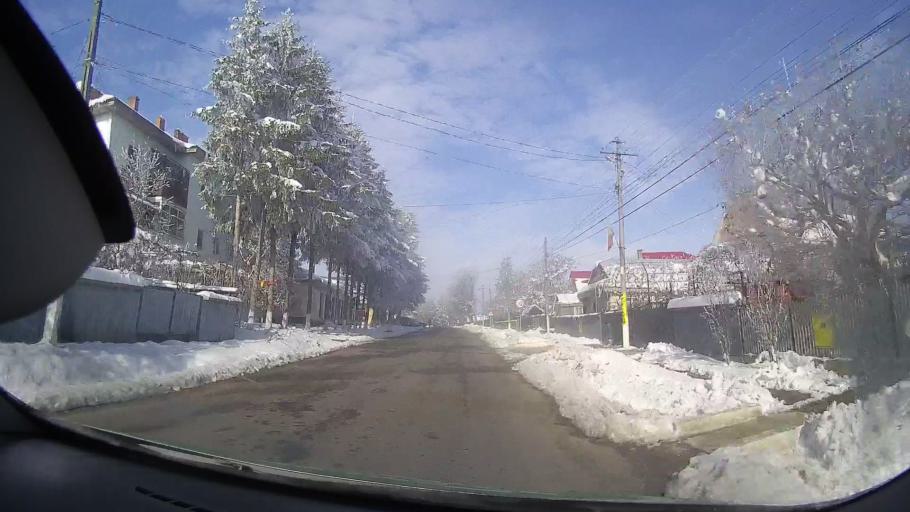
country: RO
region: Iasi
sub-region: Comuna Cristesti
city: Cristesti
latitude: 47.2581
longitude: 26.5751
